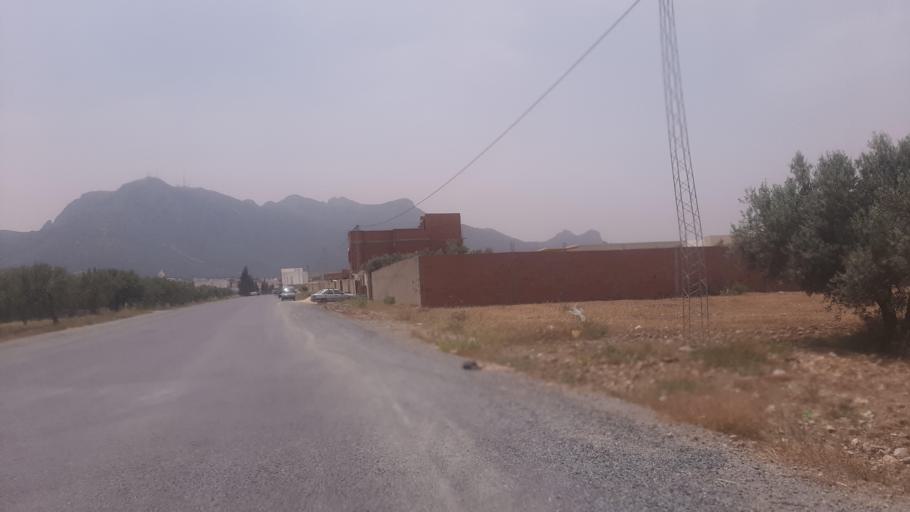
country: TN
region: Zaghwan
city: Zaghouan
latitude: 36.4180
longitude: 10.1364
